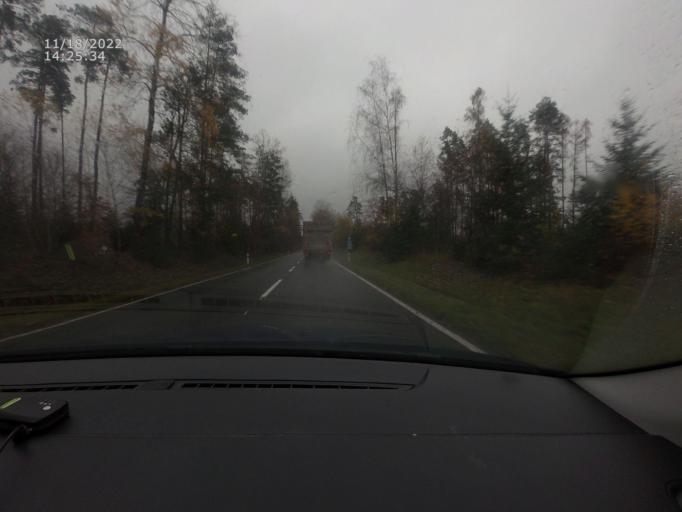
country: CZ
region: Jihocesky
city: Cimelice
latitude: 49.4337
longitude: 14.1568
